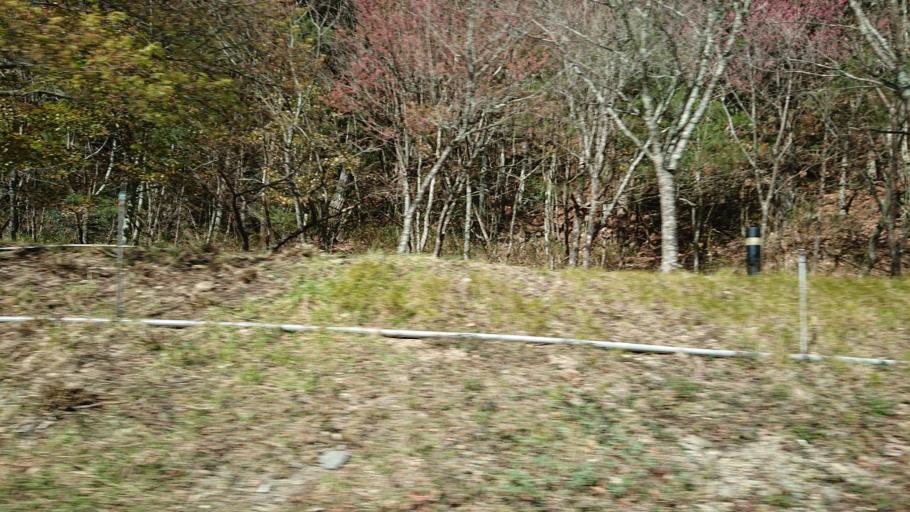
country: TW
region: Taiwan
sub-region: Hualien
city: Hualian
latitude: 24.3500
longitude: 121.3081
